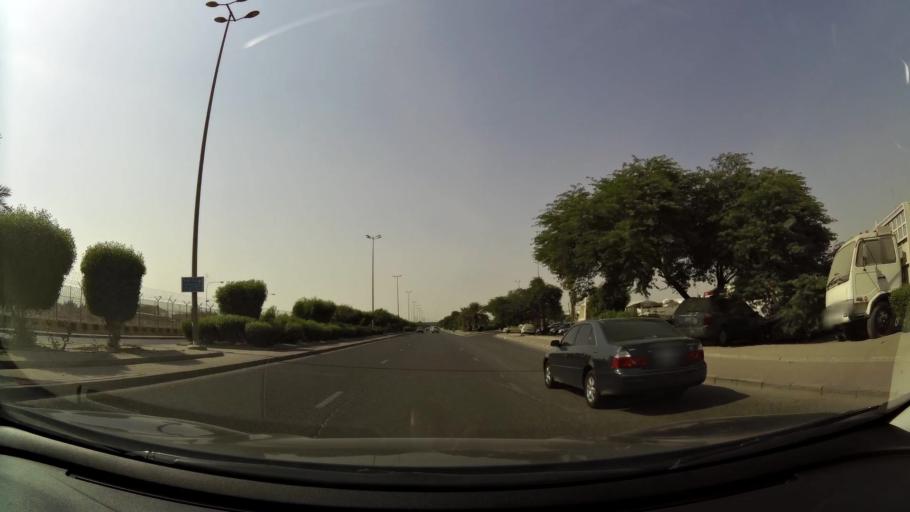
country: KW
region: Al Ahmadi
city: Al Fahahil
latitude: 29.0708
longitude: 48.1199
